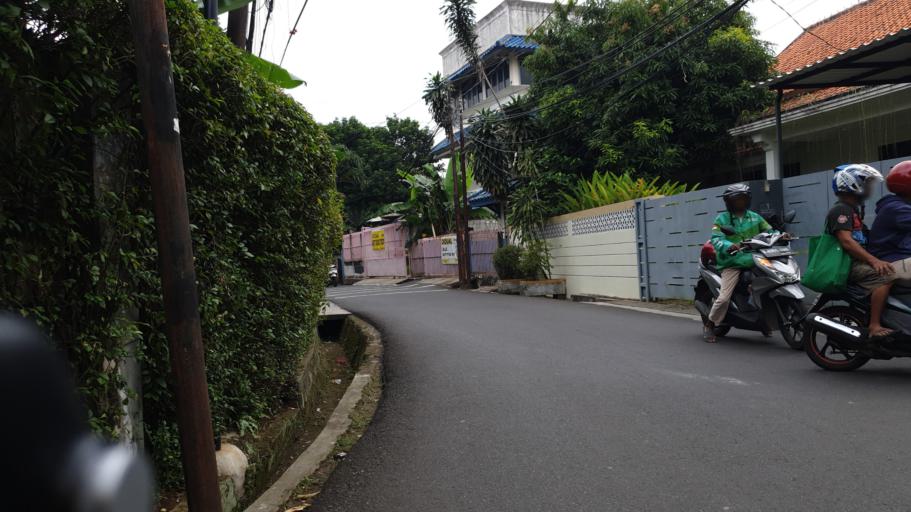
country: ID
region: Jakarta Raya
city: Jakarta
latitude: -6.2724
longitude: 106.7949
